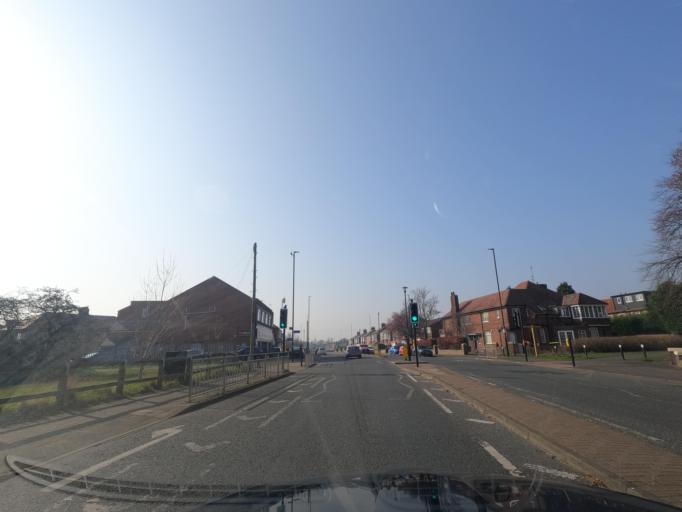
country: GB
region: England
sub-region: Newcastle upon Tyne
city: Gosforth
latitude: 55.0015
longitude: -1.5794
